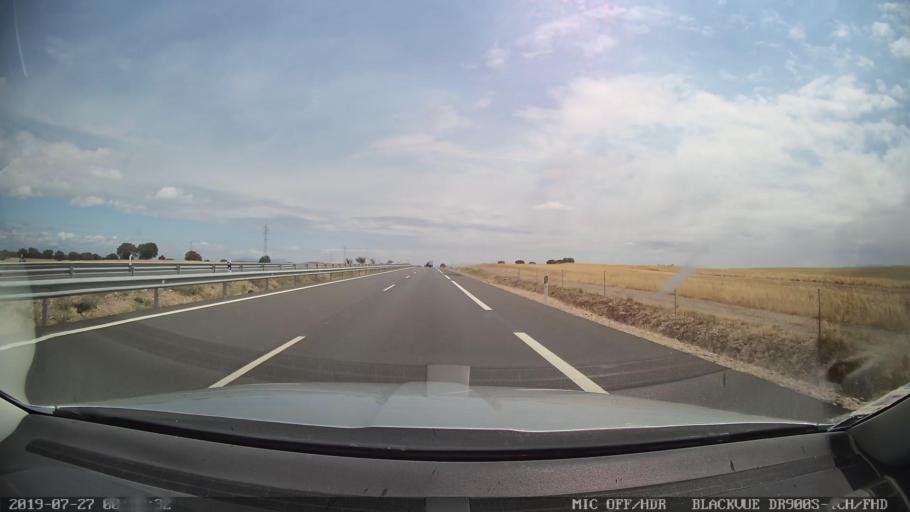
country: ES
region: Castille-La Mancha
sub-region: Province of Toledo
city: Calera y Chozas
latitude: 39.9284
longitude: -5.0150
